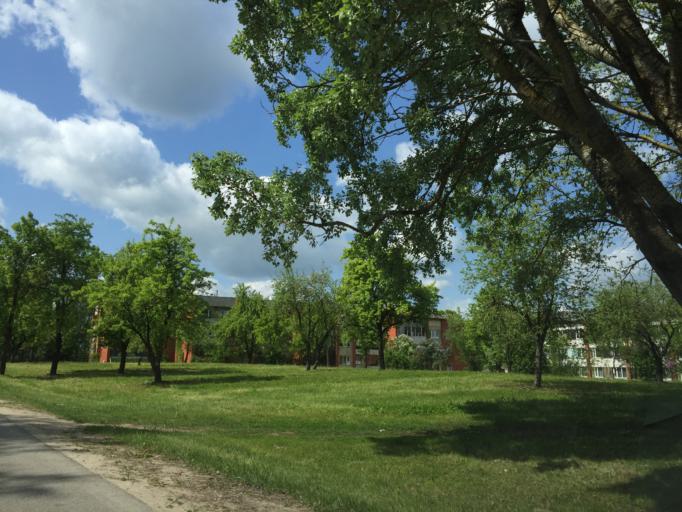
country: LV
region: Baldone
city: Baldone
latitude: 56.7387
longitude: 24.3862
